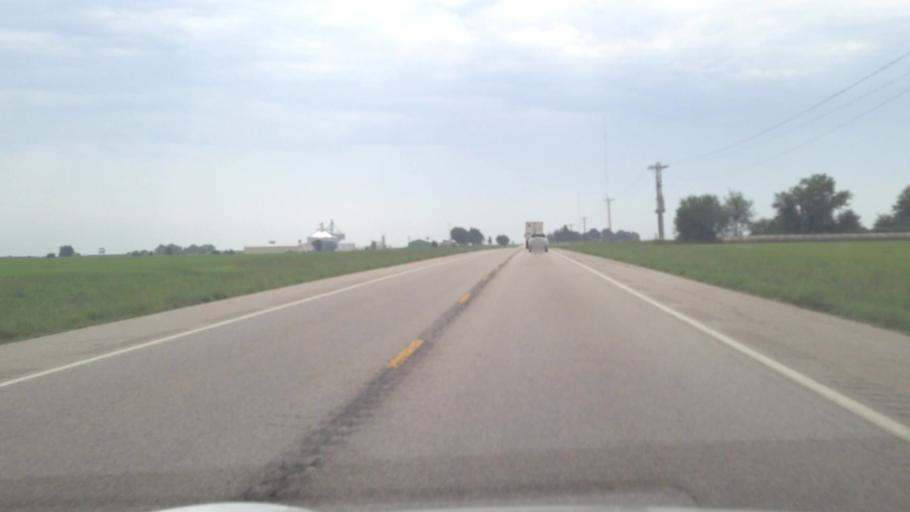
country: US
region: Missouri
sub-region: Jasper County
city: Carl Junction
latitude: 37.2440
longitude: -94.7051
